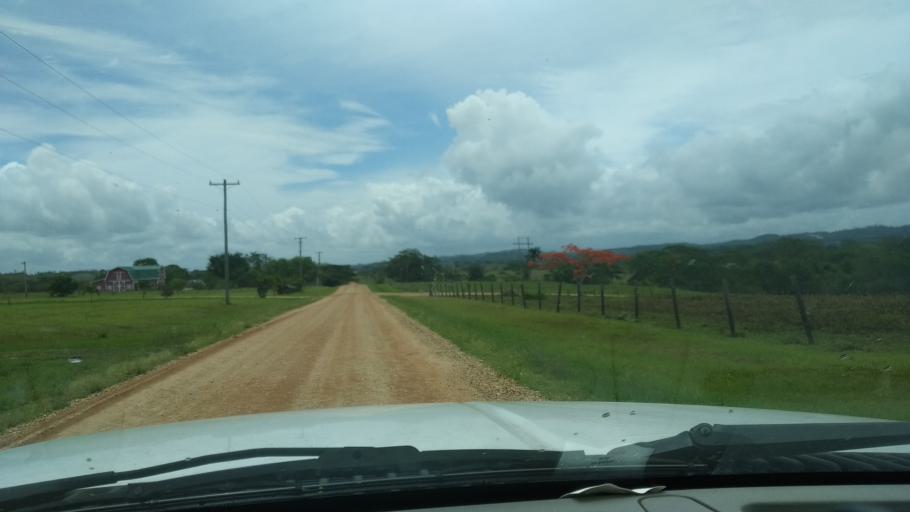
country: BZ
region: Cayo
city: San Ignacio
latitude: 17.2263
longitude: -88.9867
